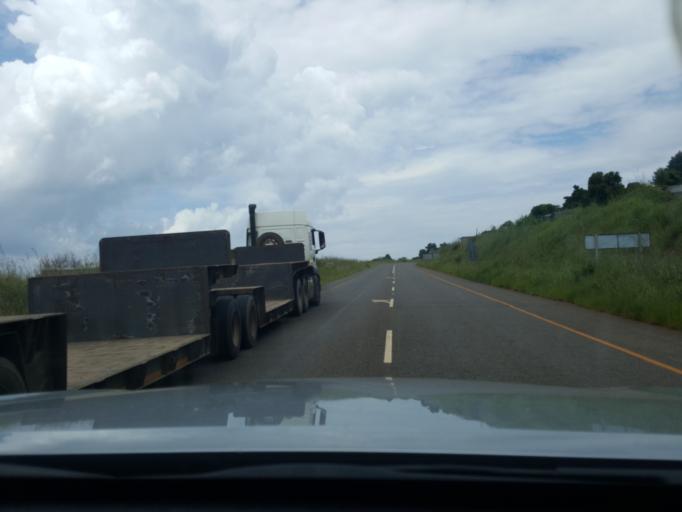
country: ZA
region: Mpumalanga
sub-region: Ehlanzeni District
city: Graksop
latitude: -25.0993
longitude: 30.7943
